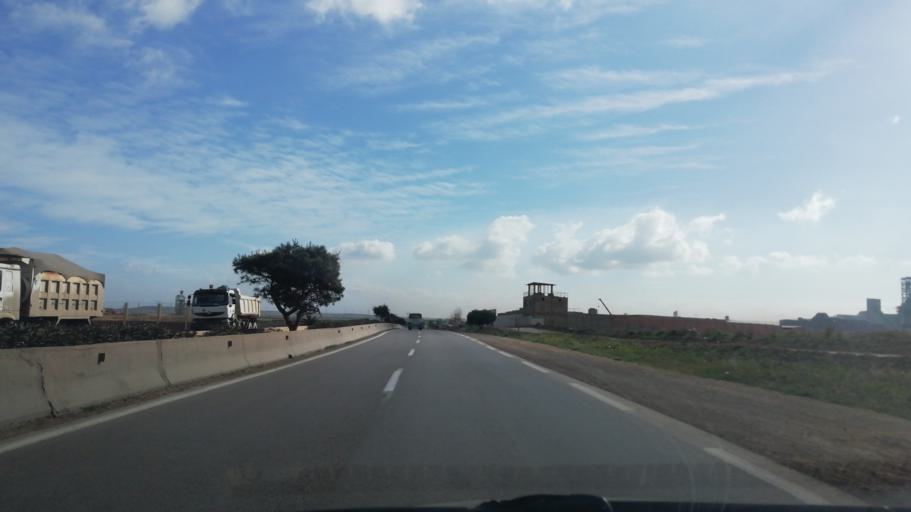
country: DZ
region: Oran
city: Ain el Bya
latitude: 35.7805
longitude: -0.2774
